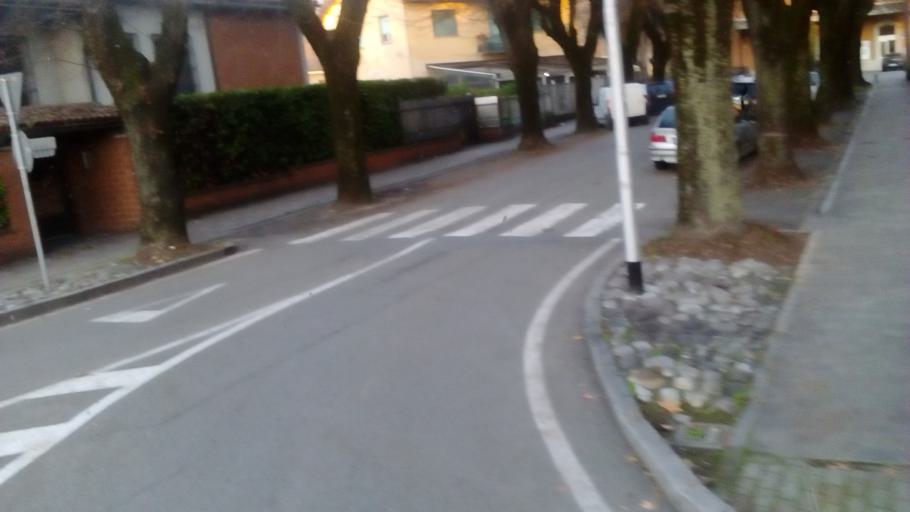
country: IT
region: Lombardy
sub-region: Provincia di Cremona
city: Castelleone
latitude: 45.3012
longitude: 9.7667
